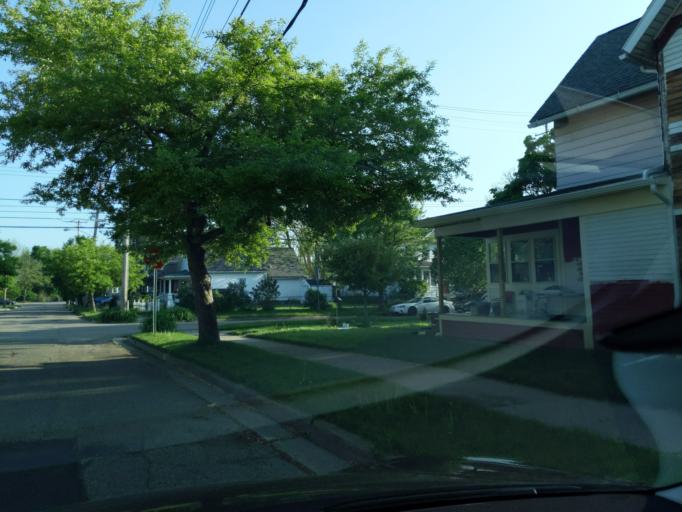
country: US
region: Michigan
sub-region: Ingham County
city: Lansing
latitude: 42.7350
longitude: -84.5291
